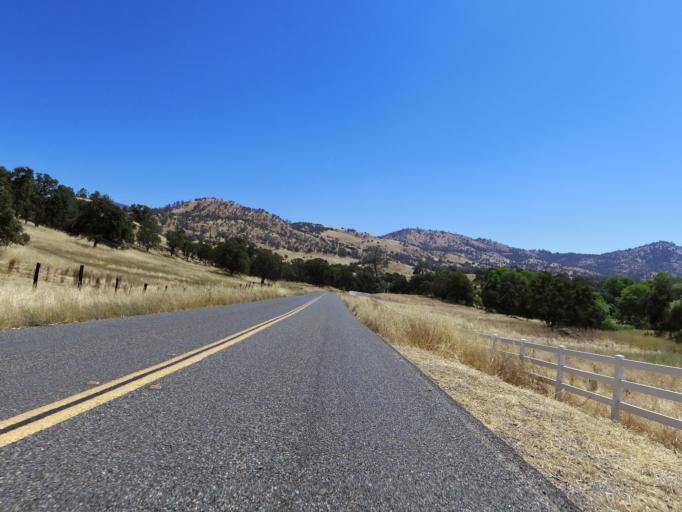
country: US
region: California
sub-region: Mariposa County
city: Mariposa
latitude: 37.4769
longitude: -120.1167
